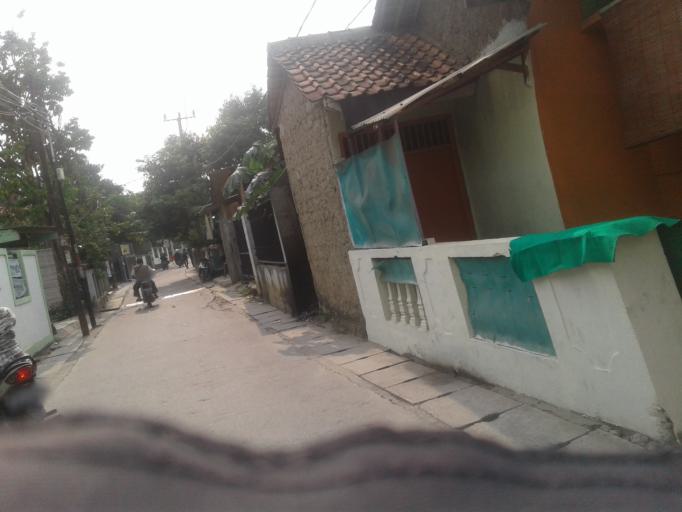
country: ID
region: West Java
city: Depok
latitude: -6.3728
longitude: 106.8376
